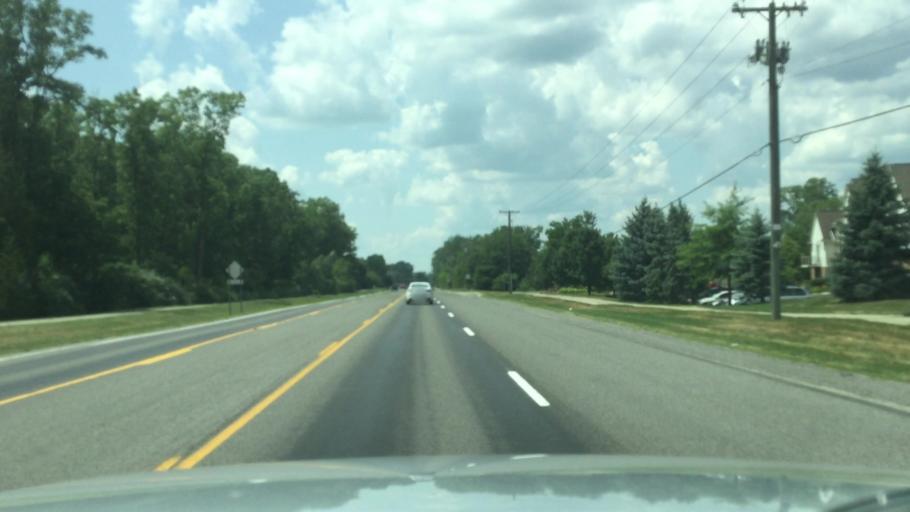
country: US
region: Michigan
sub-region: Washtenaw County
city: Ypsilanti
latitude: 42.2029
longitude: -83.5715
